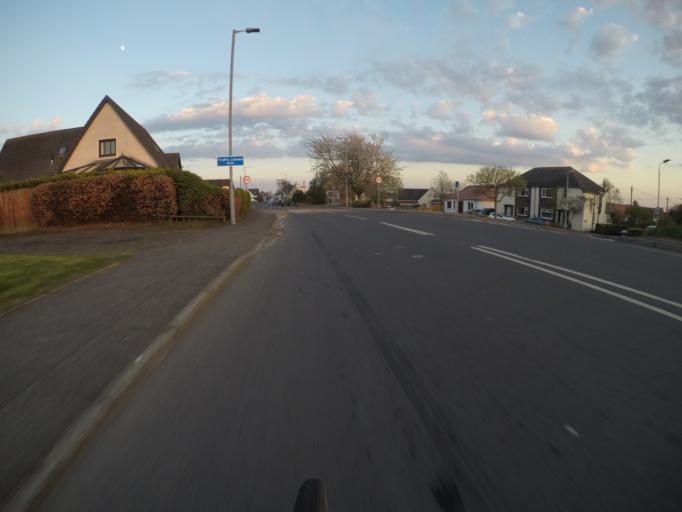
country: GB
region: Scotland
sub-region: South Ayrshire
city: Troon
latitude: 55.5529
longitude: -4.6263
